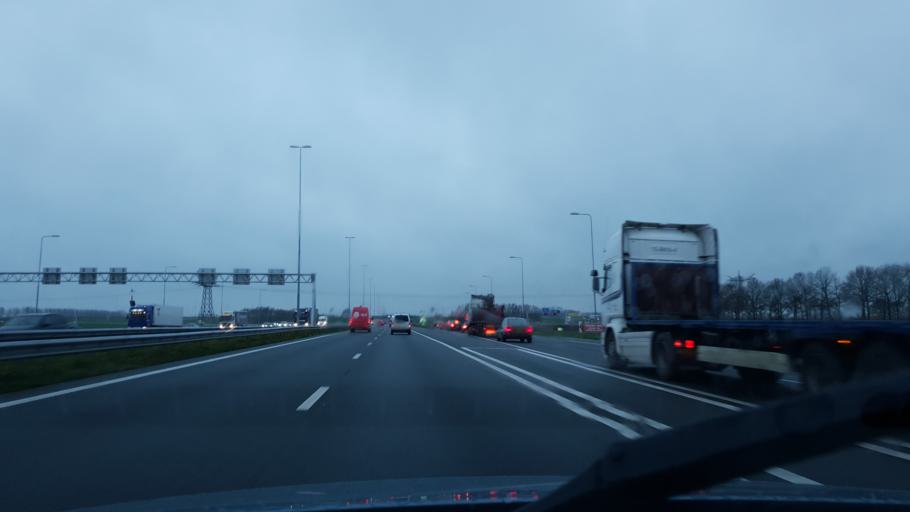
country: NL
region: Gelderland
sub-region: Gemeente Overbetuwe
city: Andelst
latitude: 51.8633
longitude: 5.7174
